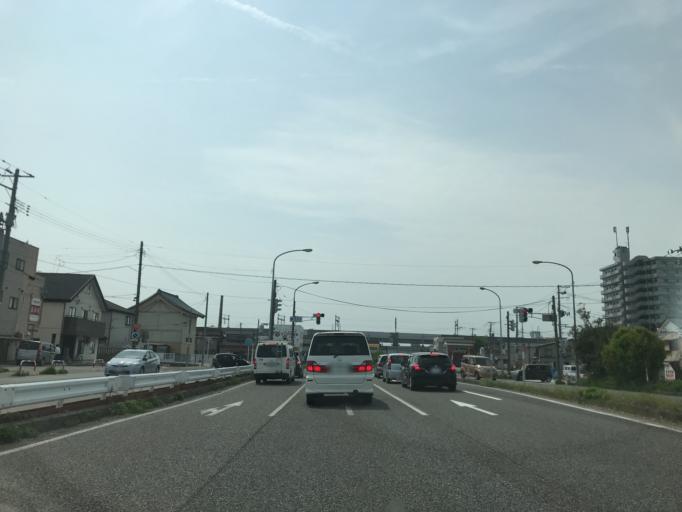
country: JP
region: Niigata
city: Niigata-shi
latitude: 37.9174
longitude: 139.0704
